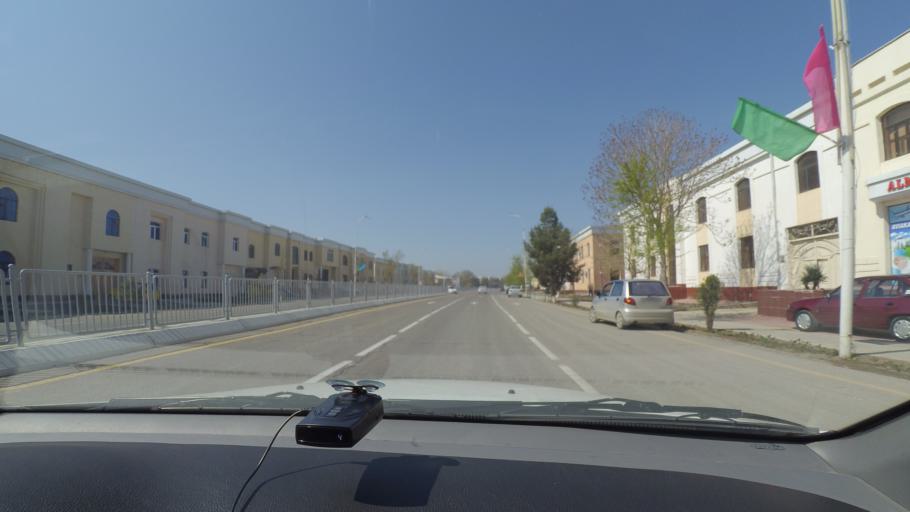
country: UZ
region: Bukhara
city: Bukhara
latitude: 39.7674
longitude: 64.4640
